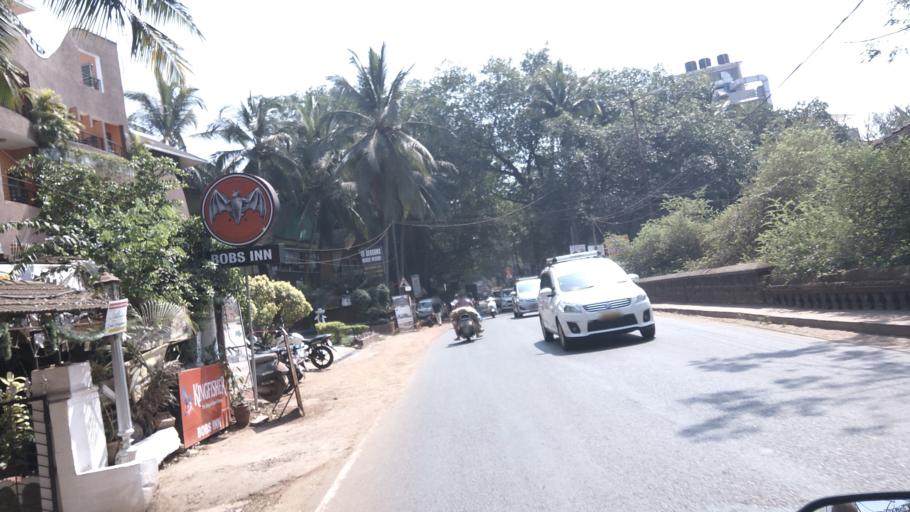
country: IN
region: Goa
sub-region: North Goa
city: Candolim
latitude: 15.5278
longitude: 73.7654
